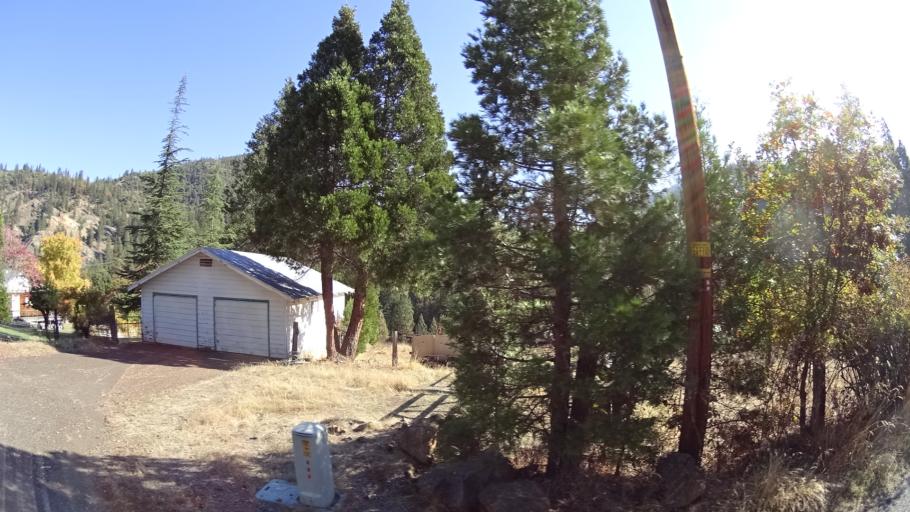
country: US
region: California
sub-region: Siskiyou County
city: Yreka
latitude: 41.7403
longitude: -123.0041
